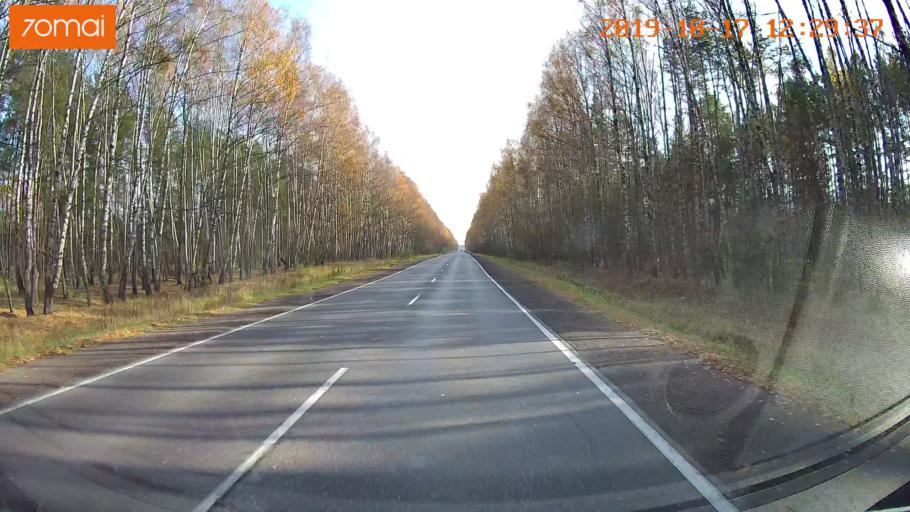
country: RU
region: Rjazan
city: Syntul
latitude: 54.9804
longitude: 41.2963
